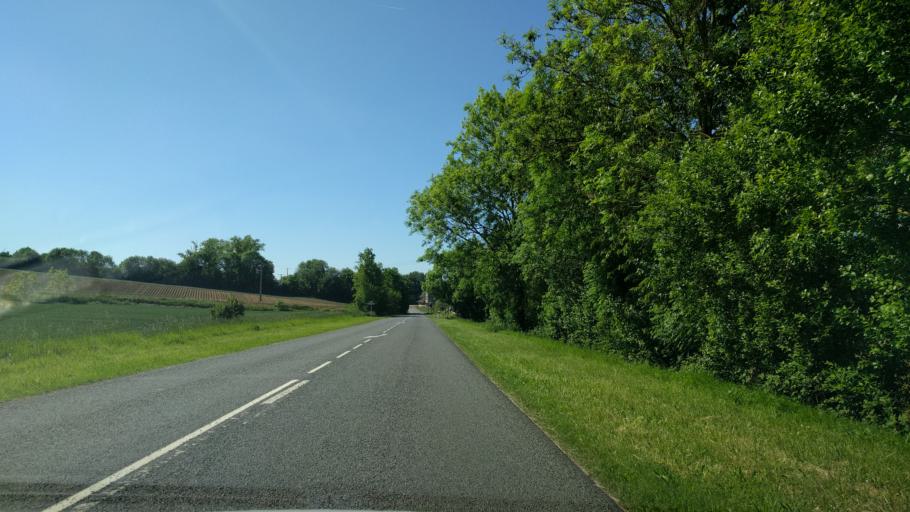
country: FR
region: Picardie
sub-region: Departement de la Somme
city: Peronne
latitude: 49.9179
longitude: 2.9245
